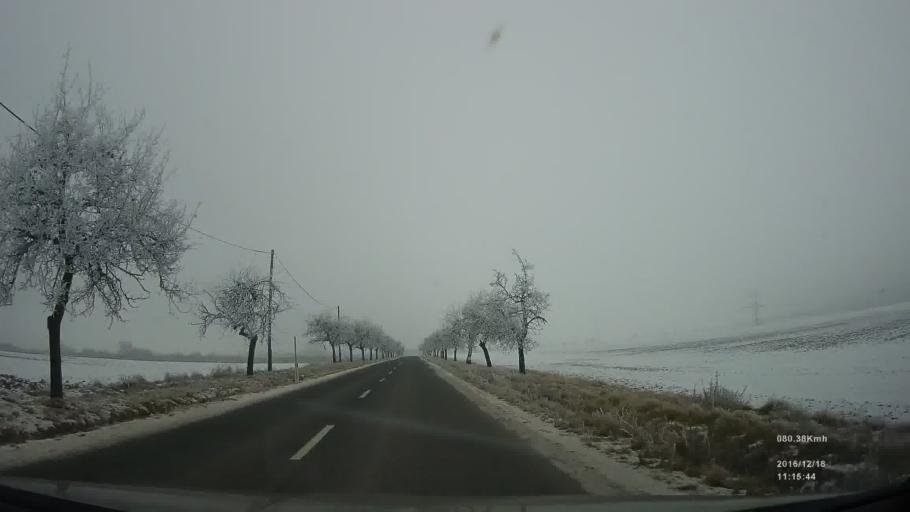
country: SK
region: Presovsky
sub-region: Okres Presov
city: Presov
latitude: 48.9087
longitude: 21.3248
